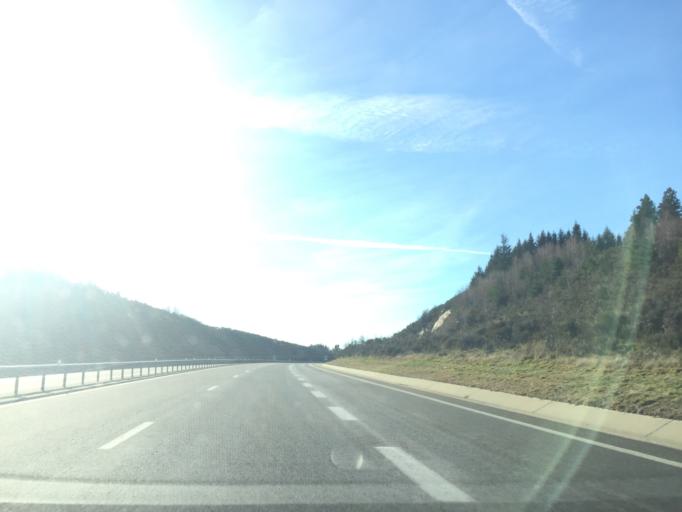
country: FR
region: Auvergne
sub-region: Departement du Puy-de-Dome
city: Gelles
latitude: 45.7976
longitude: 2.7657
